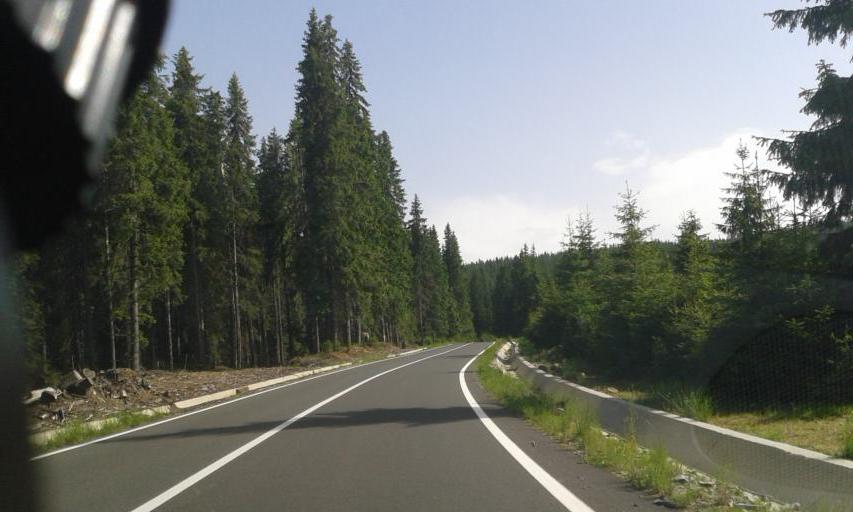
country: RO
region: Hunedoara
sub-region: Oras Petrila
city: Petrila
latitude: 45.4860
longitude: 23.6398
